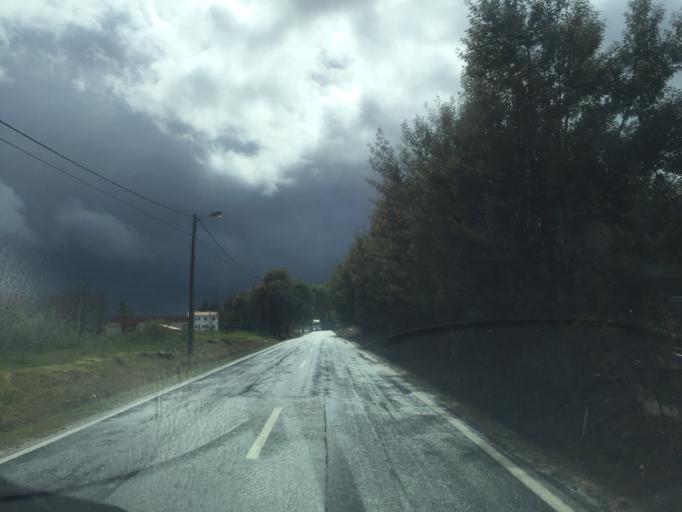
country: PT
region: Guarda
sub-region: Seia
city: Seia
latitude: 40.4176
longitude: -7.7394
